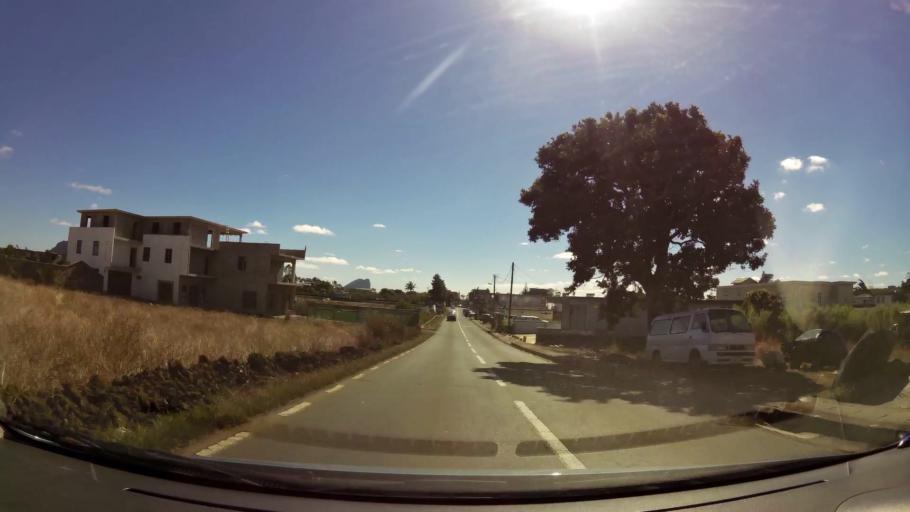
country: MU
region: Plaines Wilhems
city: Vacoas
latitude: -20.3297
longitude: 57.4865
